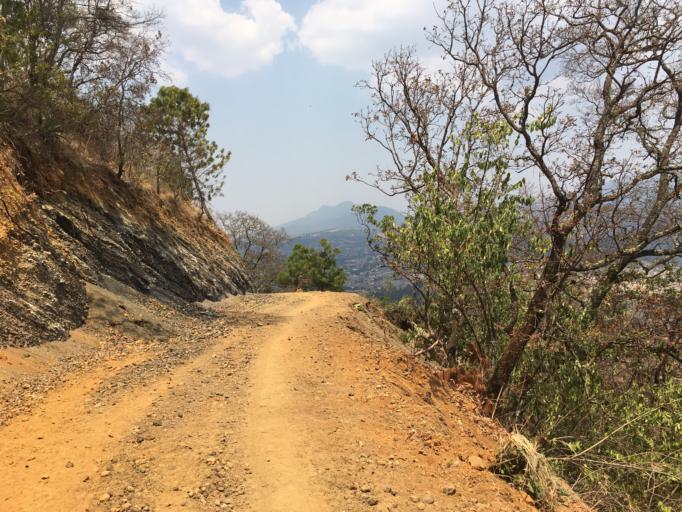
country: MX
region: Michoacan
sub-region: Patzcuaro
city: Santa Ana Chapitiro
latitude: 19.5101
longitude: -101.6393
